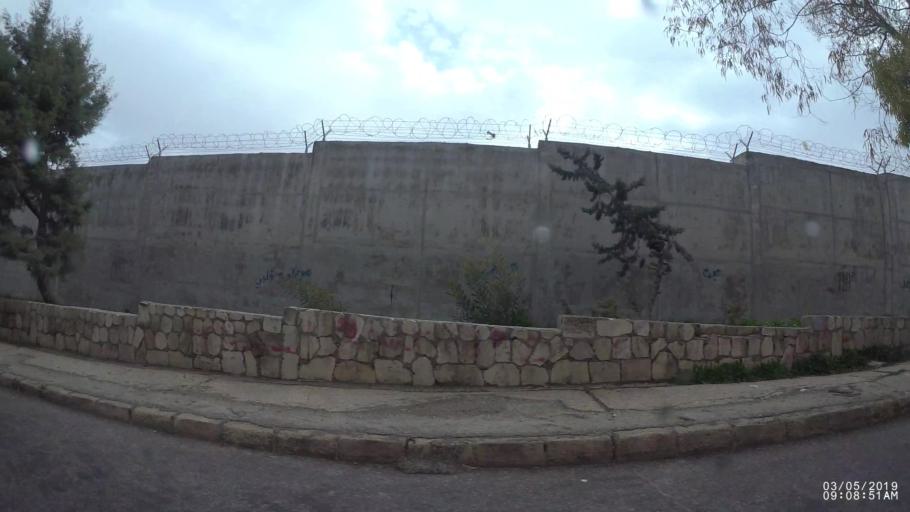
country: JO
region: Amman
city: Amman
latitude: 31.9645
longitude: 35.9363
